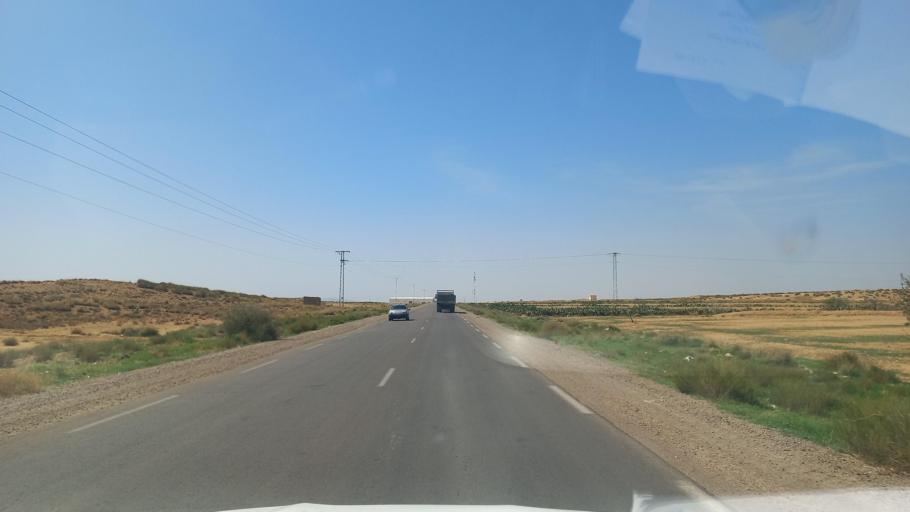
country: TN
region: Al Qasrayn
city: Sbiba
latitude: 35.3820
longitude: 9.1098
